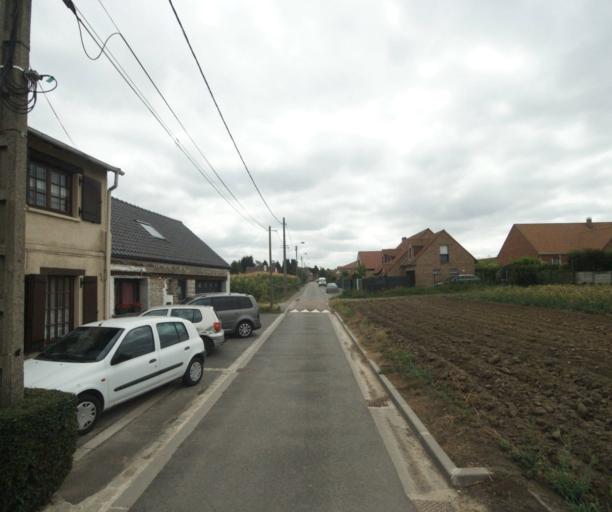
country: FR
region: Nord-Pas-de-Calais
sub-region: Departement du Nord
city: Toufflers
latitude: 50.6647
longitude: 3.2314
